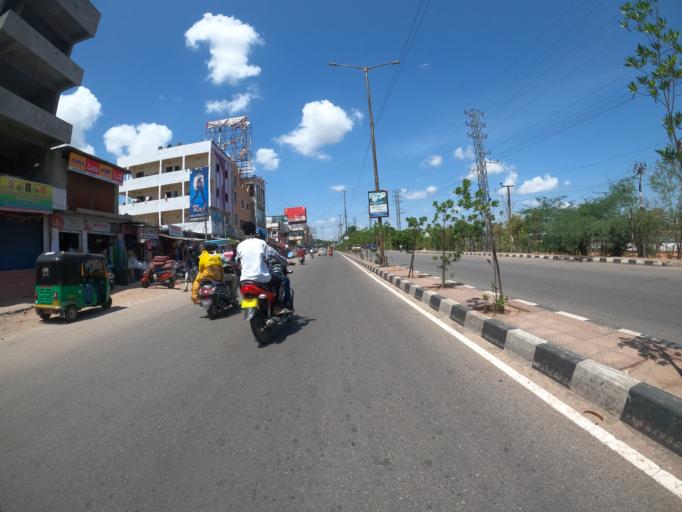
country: IN
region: Telangana
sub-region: Hyderabad
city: Hyderabad
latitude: 17.3540
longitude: 78.3784
